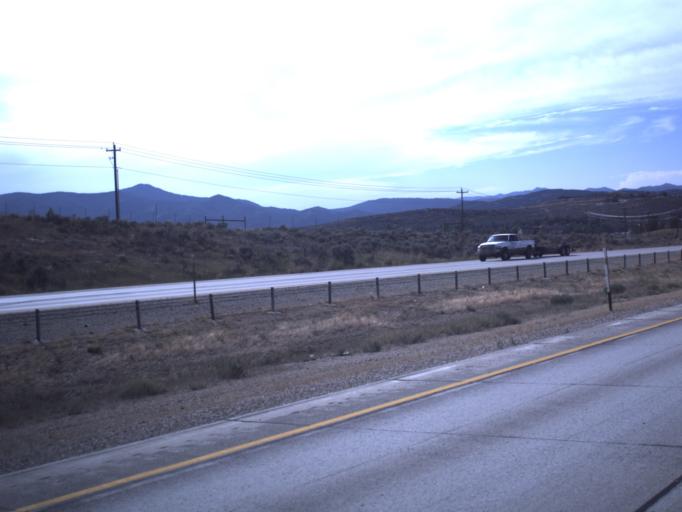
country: US
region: Utah
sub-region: Summit County
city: Snyderville
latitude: 40.7098
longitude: -111.4806
